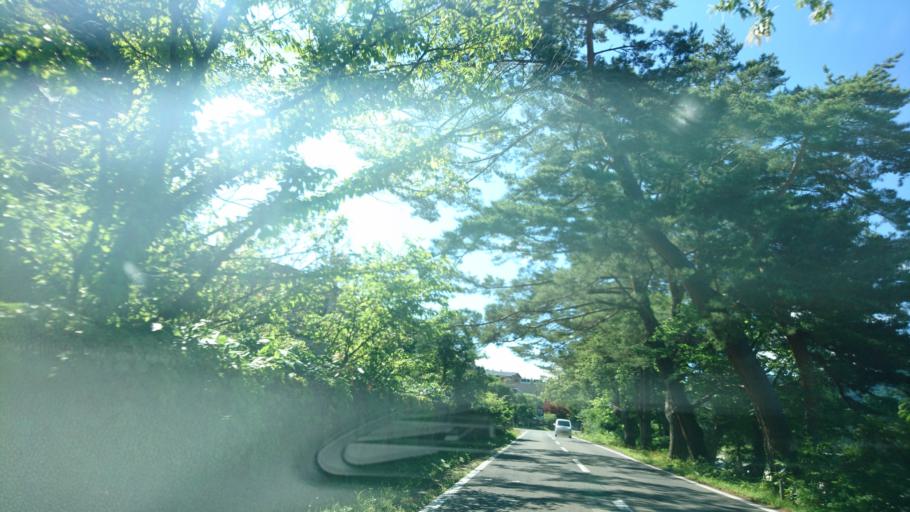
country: JP
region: Akita
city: Kakunodatemachi
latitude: 39.7360
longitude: 140.6962
